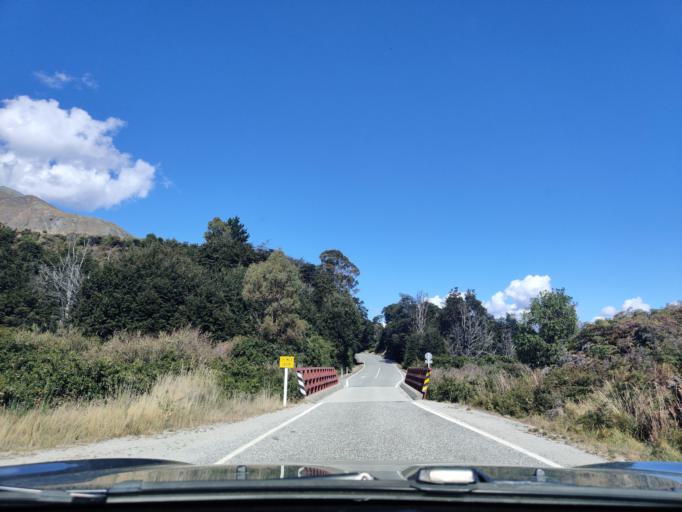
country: NZ
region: Otago
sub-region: Queenstown-Lakes District
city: Queenstown
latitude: -44.9912
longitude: 168.4319
